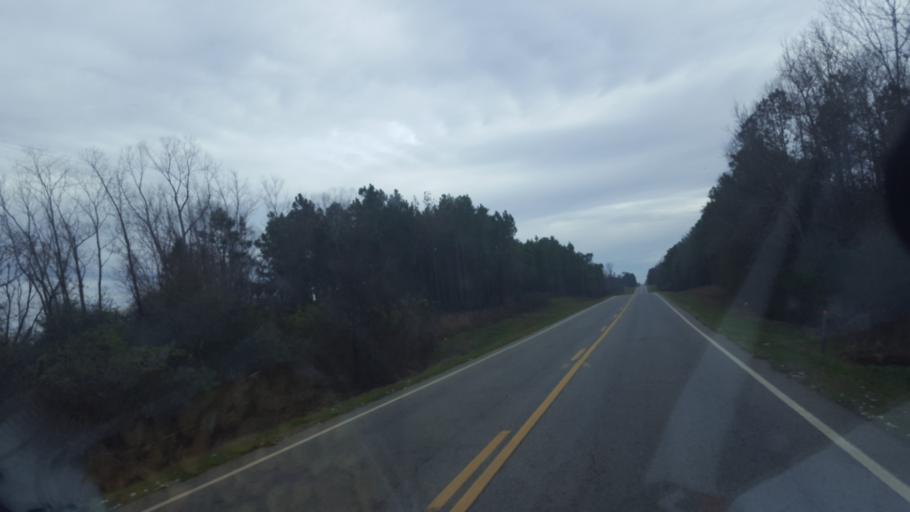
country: US
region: Georgia
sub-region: Turner County
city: Ashburn
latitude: 31.7619
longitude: -83.5427
